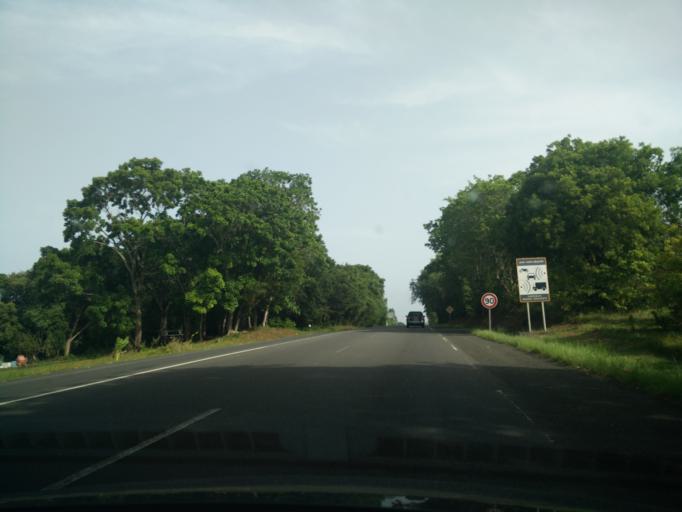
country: GP
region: Guadeloupe
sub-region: Guadeloupe
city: Petit-Bourg
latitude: 16.1443
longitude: -61.5827
